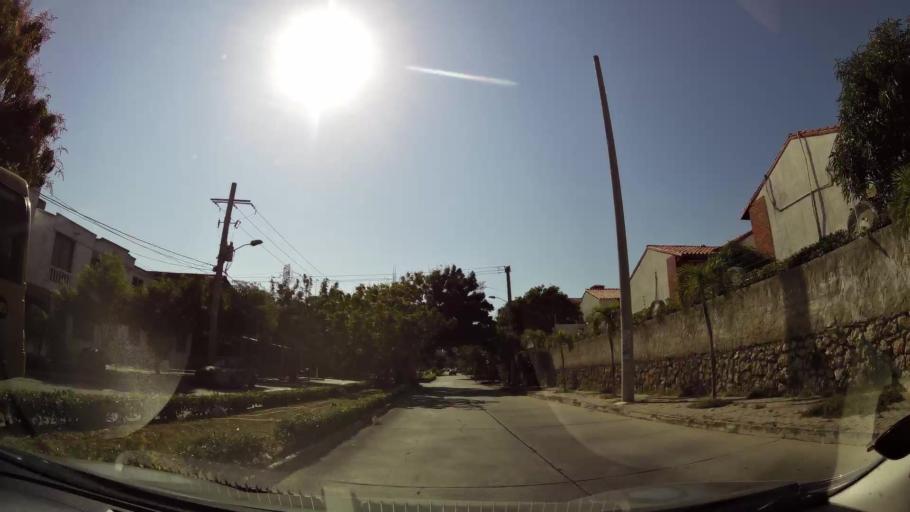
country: CO
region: Atlantico
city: Barranquilla
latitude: 11.0242
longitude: -74.8130
